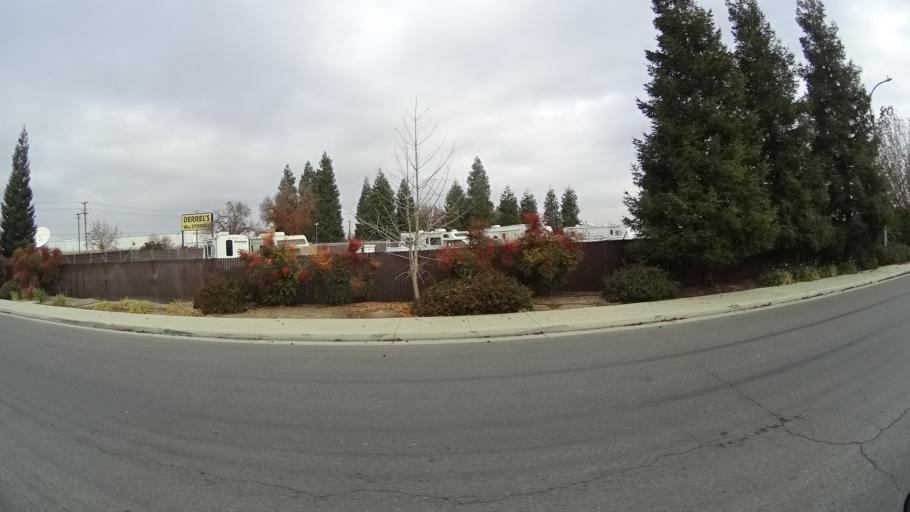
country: US
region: California
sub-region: Kern County
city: Greenfield
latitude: 35.3085
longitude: -119.0738
